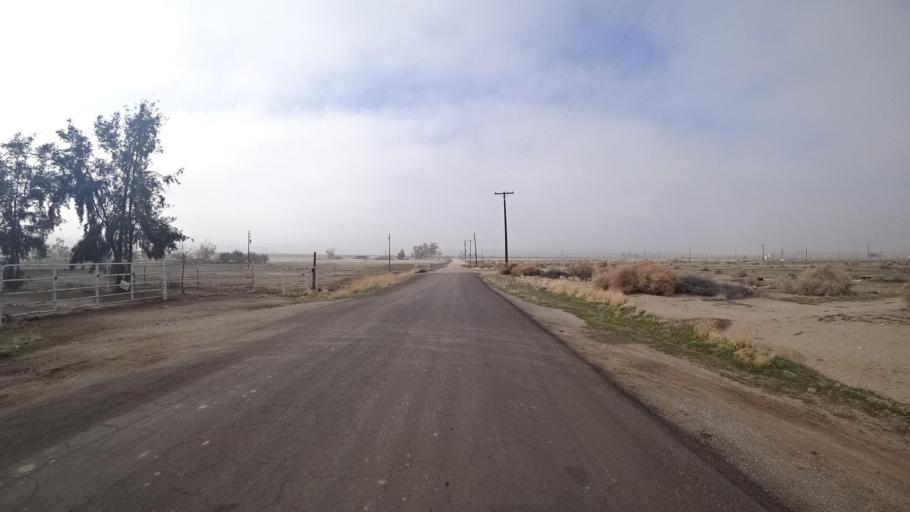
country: US
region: California
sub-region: Kern County
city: Maricopa
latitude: 35.0469
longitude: -119.3544
